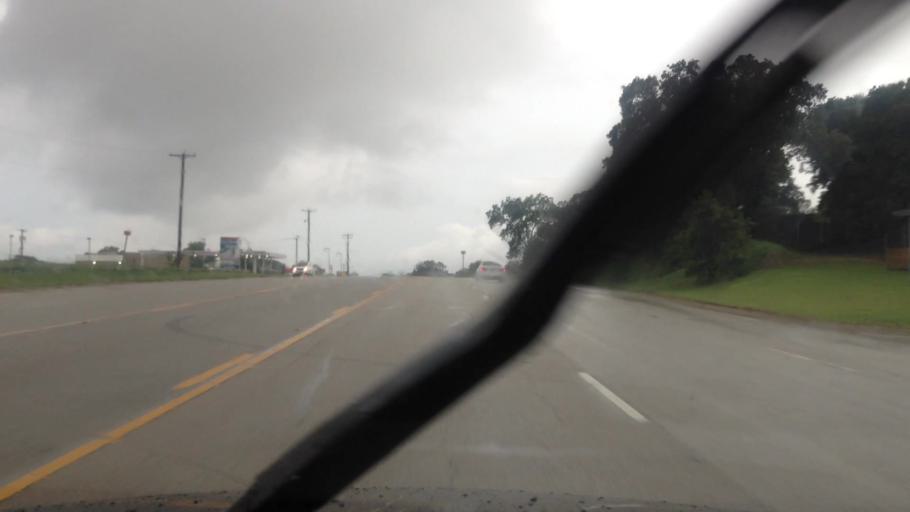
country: US
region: Texas
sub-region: Tarrant County
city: North Richland Hills
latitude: 32.8727
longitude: -97.2073
